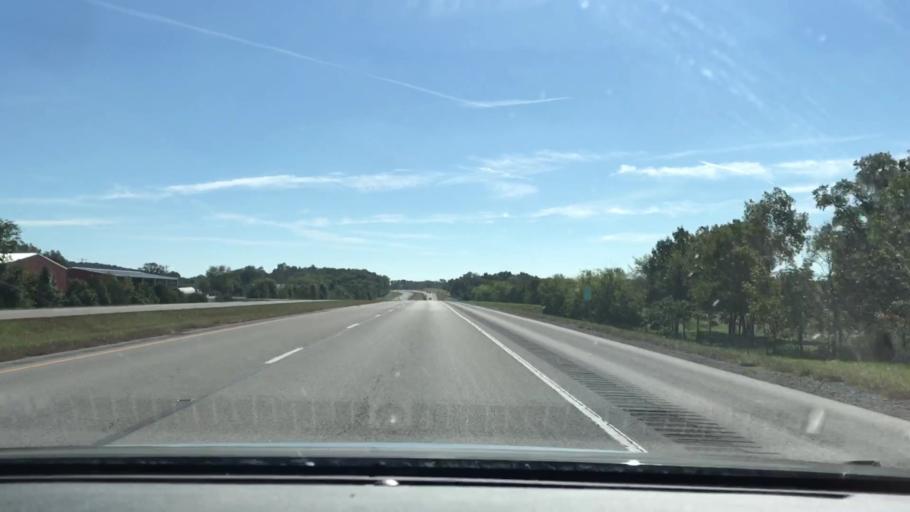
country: US
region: Kentucky
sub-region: Todd County
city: Elkton
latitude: 36.8331
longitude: -87.2316
